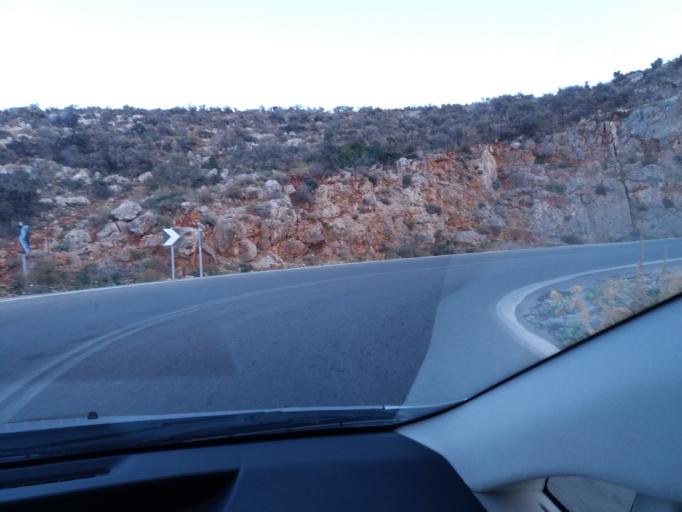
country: GR
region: Crete
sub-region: Nomos Irakleiou
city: Mokhos
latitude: 35.2750
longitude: 25.4291
